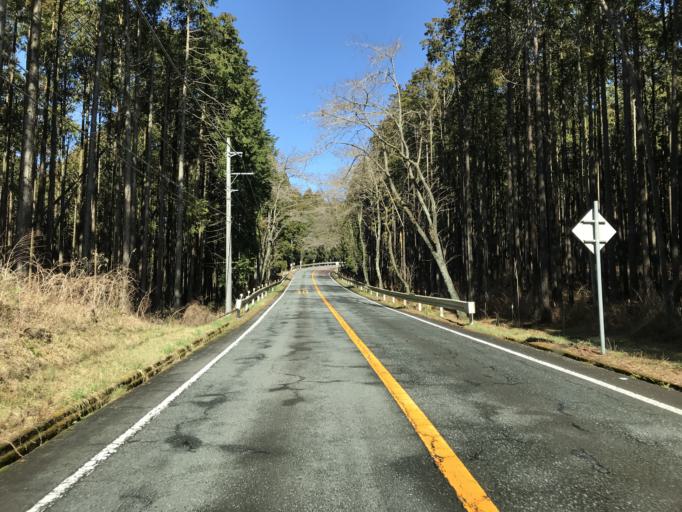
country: JP
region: Shizuoka
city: Fujinomiya
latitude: 35.2891
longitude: 138.6624
